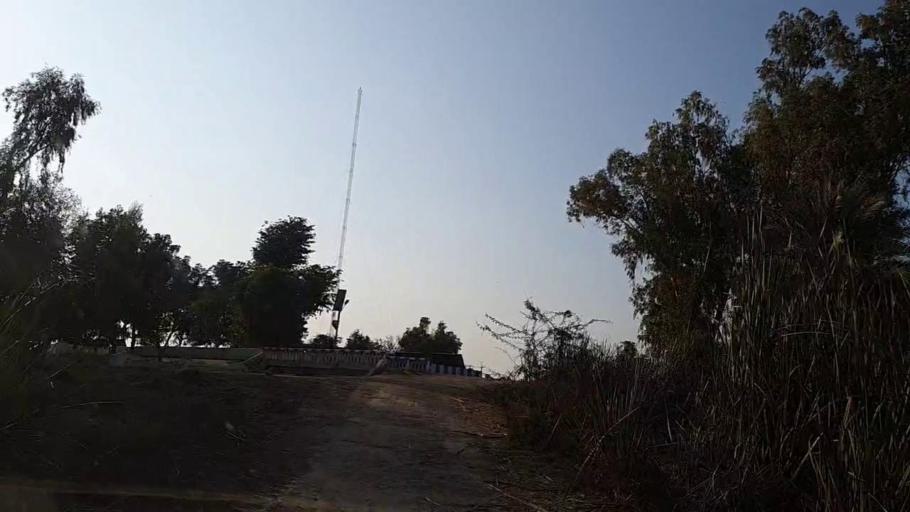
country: PK
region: Sindh
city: Sakrand
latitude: 26.0940
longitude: 68.3735
